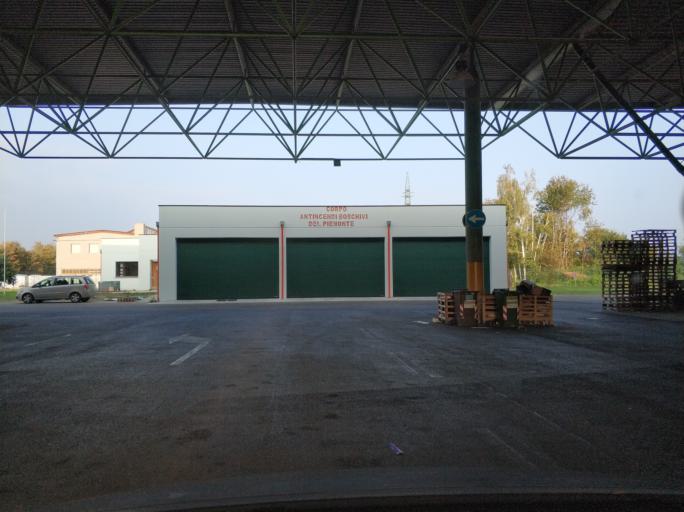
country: IT
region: Piedmont
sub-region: Provincia di Biella
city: Gaglianico
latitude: 45.5502
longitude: 8.0791
